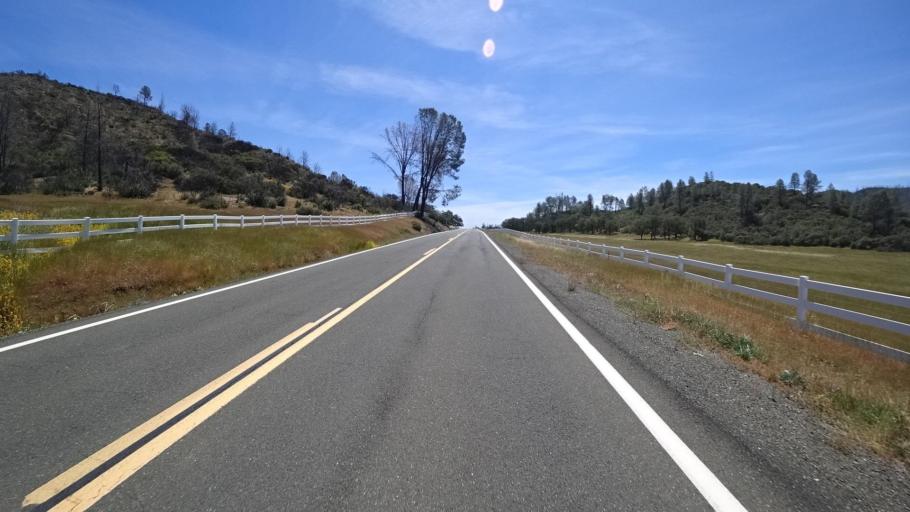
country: US
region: California
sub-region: Lake County
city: Hidden Valley Lake
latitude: 38.7217
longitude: -122.5054
